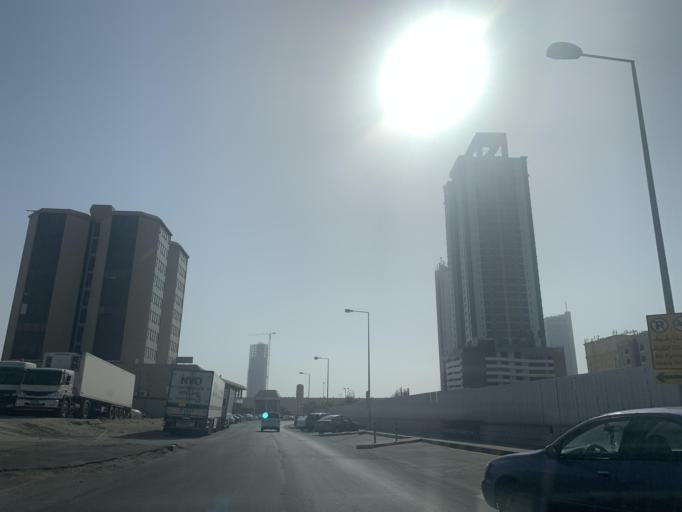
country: BH
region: Manama
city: Manama
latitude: 26.2326
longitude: 50.5685
